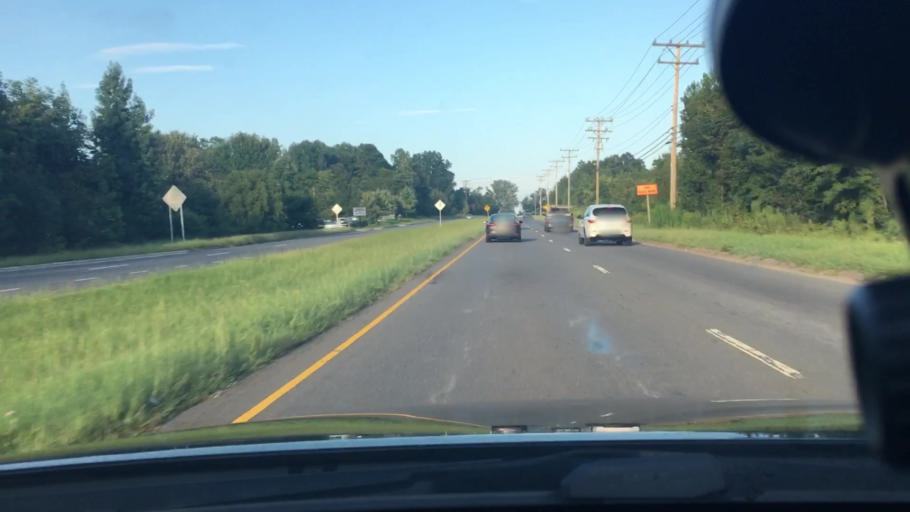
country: US
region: North Carolina
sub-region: Mecklenburg County
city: Mint Hill
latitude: 35.2231
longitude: -80.6399
